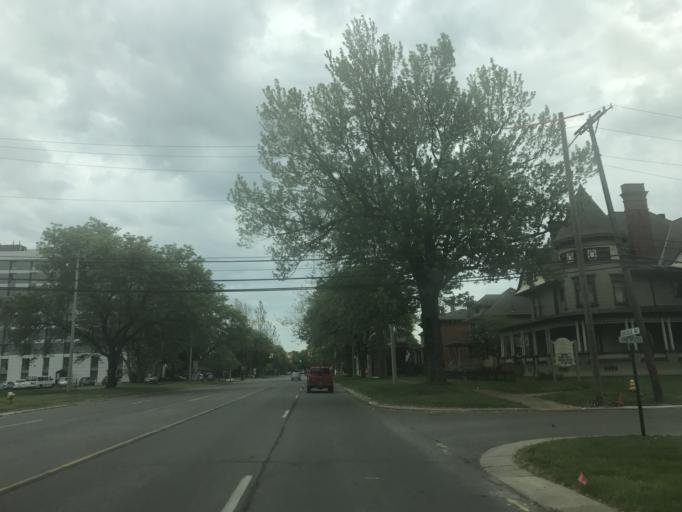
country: US
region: Michigan
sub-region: Wayne County
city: Wyandotte
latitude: 42.2079
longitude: -83.1485
